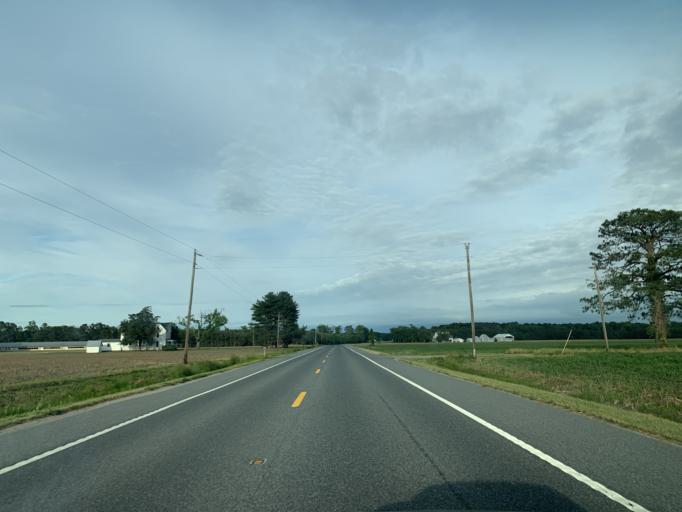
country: US
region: Virginia
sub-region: Accomack County
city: Captains Cove
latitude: 38.0696
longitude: -75.4475
